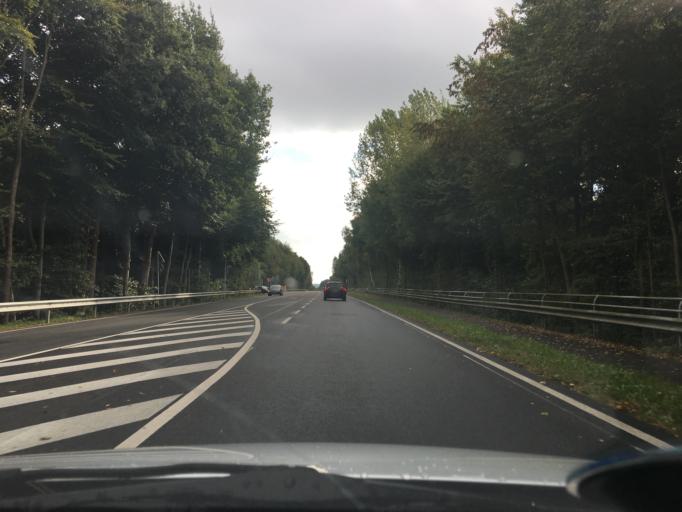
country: DE
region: Lower Saxony
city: Wallenhorst
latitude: 52.3955
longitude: 8.0338
